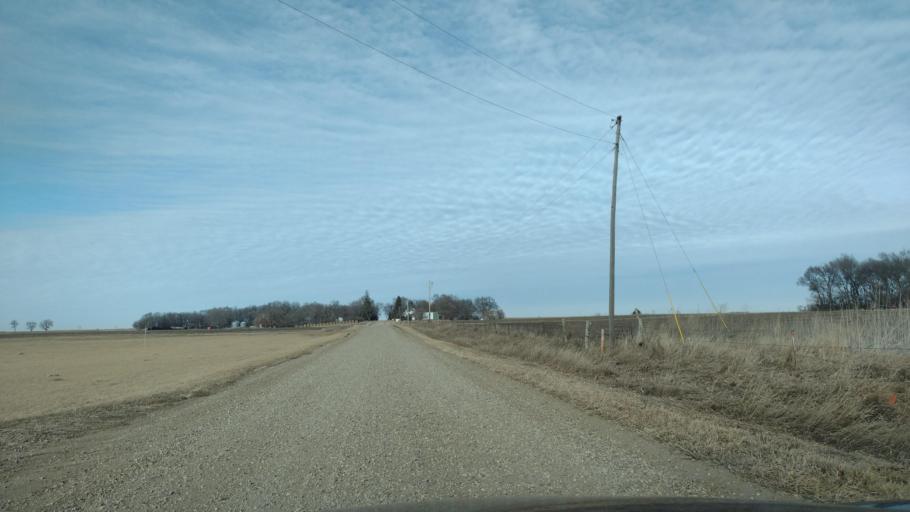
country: US
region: South Dakota
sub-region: Union County
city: Beresford
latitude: 42.9569
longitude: -96.8055
